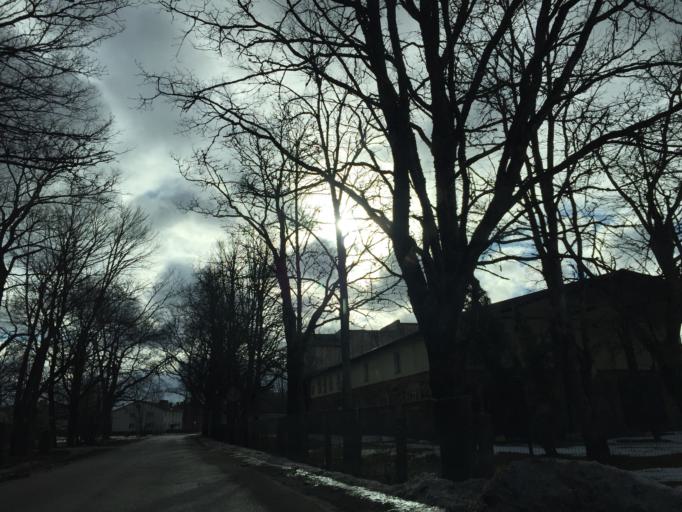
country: LV
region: Aloja
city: Aloja
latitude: 57.7727
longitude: 24.8129
